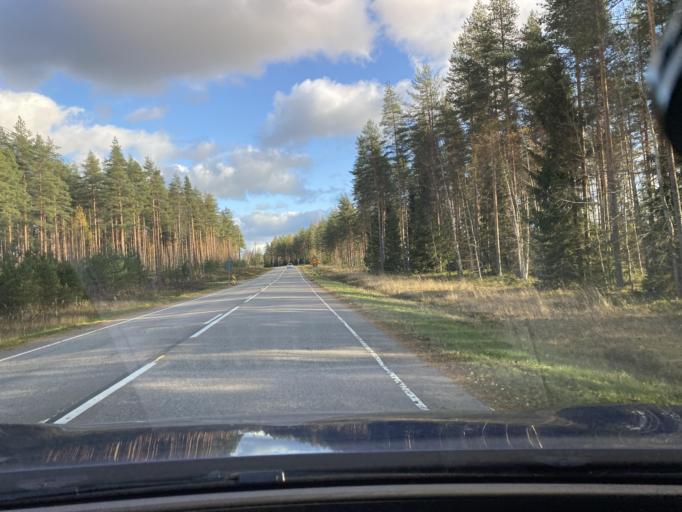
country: FI
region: Paijanne Tavastia
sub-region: Lahti
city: Jaervelae
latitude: 60.8426
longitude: 25.3113
